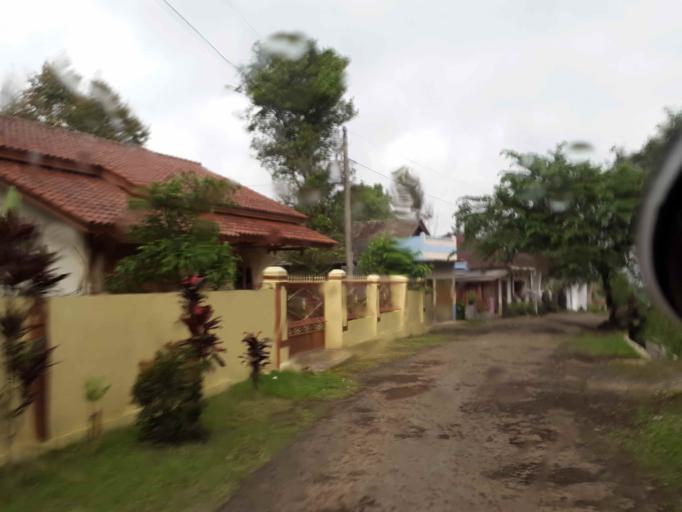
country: ID
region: Central Java
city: Lebaksiu
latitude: -7.1420
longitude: 109.1944
